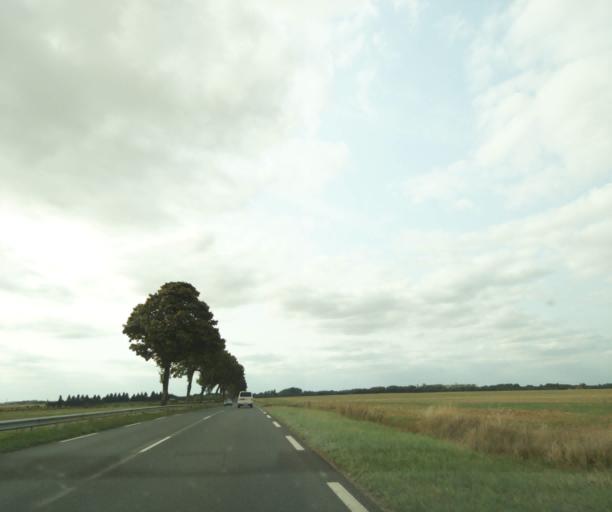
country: FR
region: Centre
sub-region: Departement d'Indre-et-Loire
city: Reignac-sur-Indre
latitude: 47.2022
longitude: 0.9112
